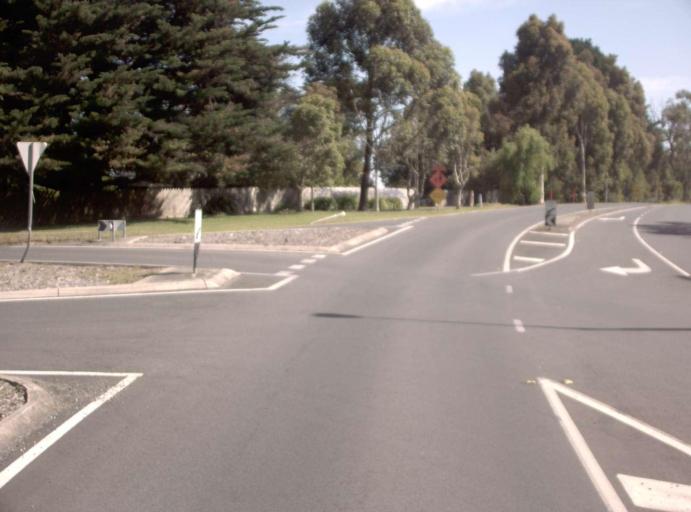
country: AU
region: Victoria
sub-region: Baw Baw
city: Warragul
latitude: -38.1697
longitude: 145.8282
